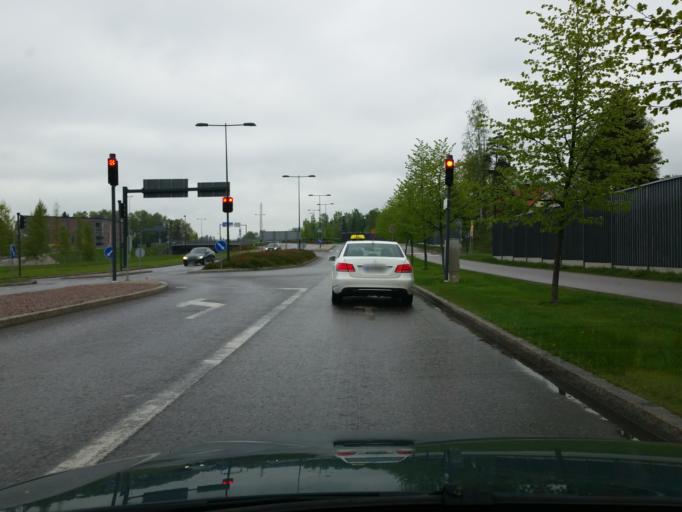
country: FI
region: Uusimaa
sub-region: Helsinki
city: Teekkarikylae
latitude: 60.2249
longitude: 24.8259
